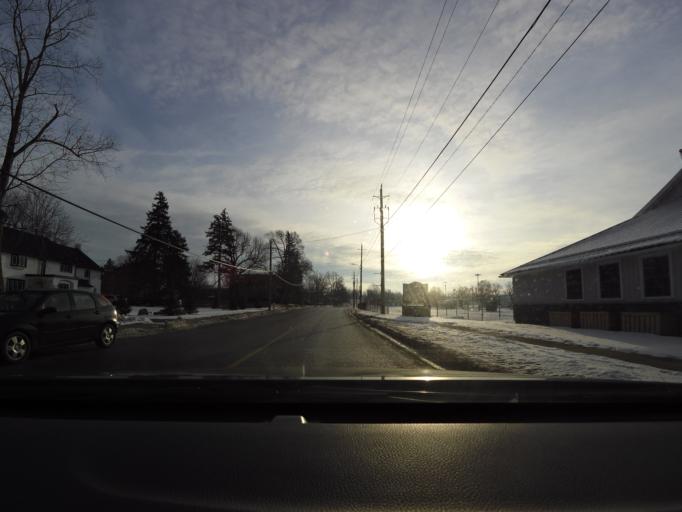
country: CA
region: Ontario
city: Ancaster
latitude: 43.0726
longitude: -79.9474
